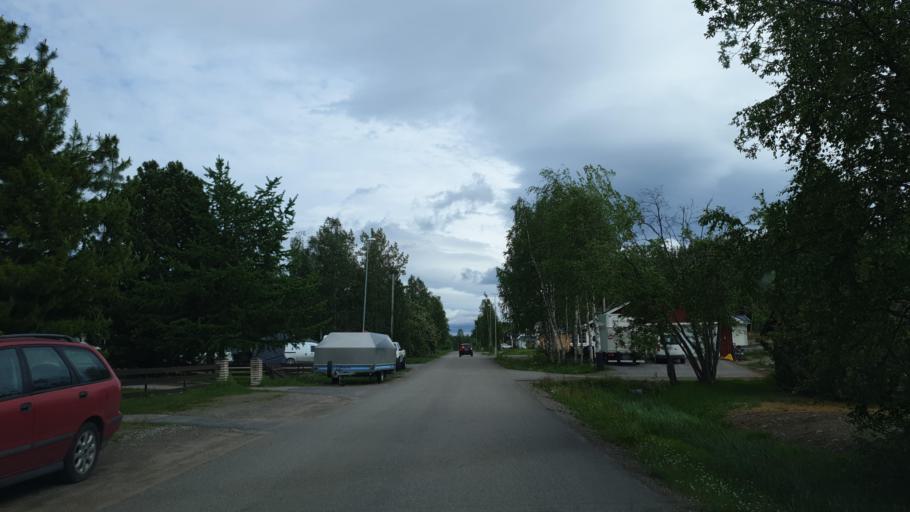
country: SE
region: Norrbotten
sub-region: Gallivare Kommun
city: Gaellivare
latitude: 67.1320
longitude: 20.6315
